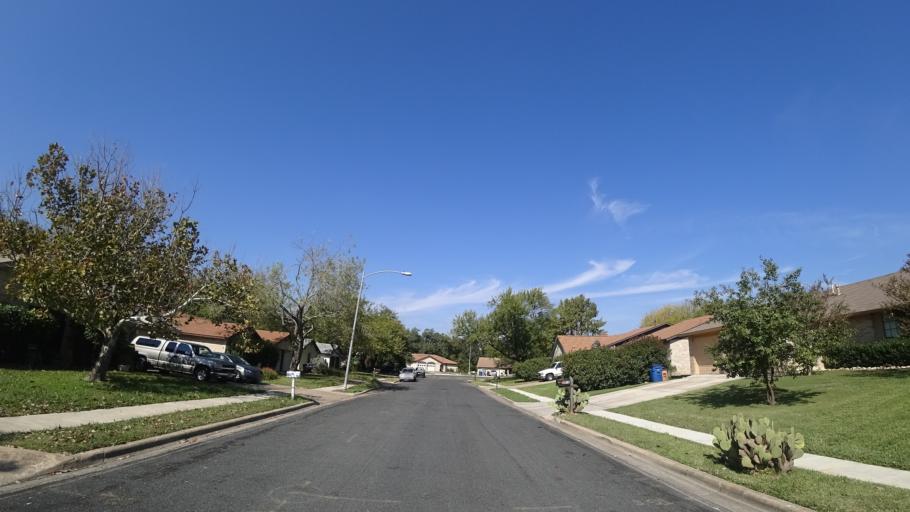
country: US
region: Texas
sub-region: Travis County
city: Shady Hollow
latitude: 30.2139
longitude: -97.8192
